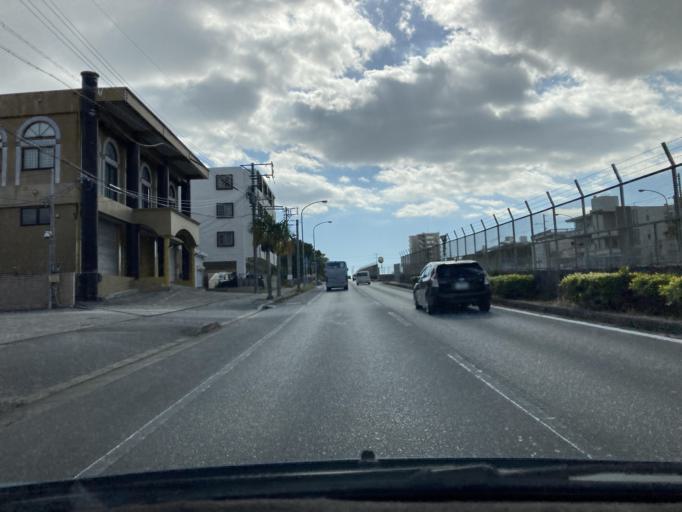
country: JP
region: Okinawa
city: Okinawa
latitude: 26.3290
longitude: 127.7857
